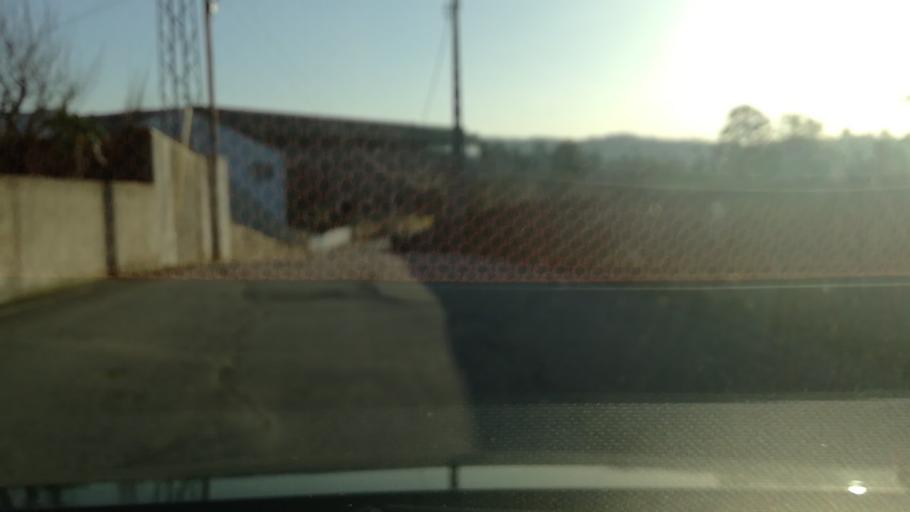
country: PT
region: Porto
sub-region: Trofa
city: Bougado
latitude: 41.3399
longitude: -8.5266
